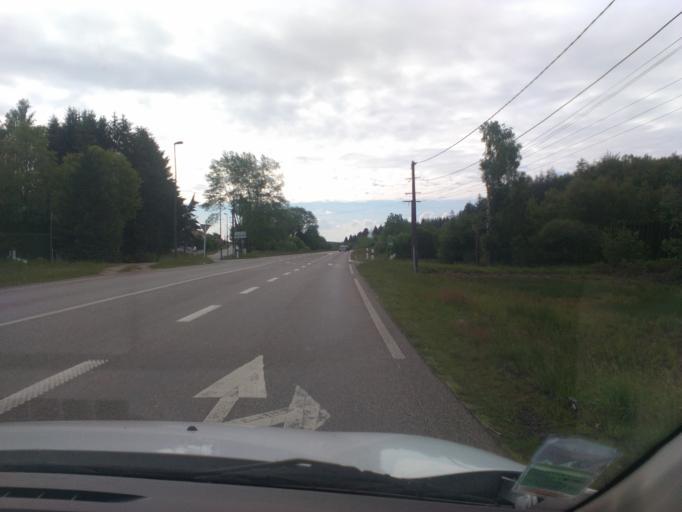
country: FR
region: Lorraine
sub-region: Departement des Vosges
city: Deyvillers
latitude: 48.1715
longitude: 6.5187
